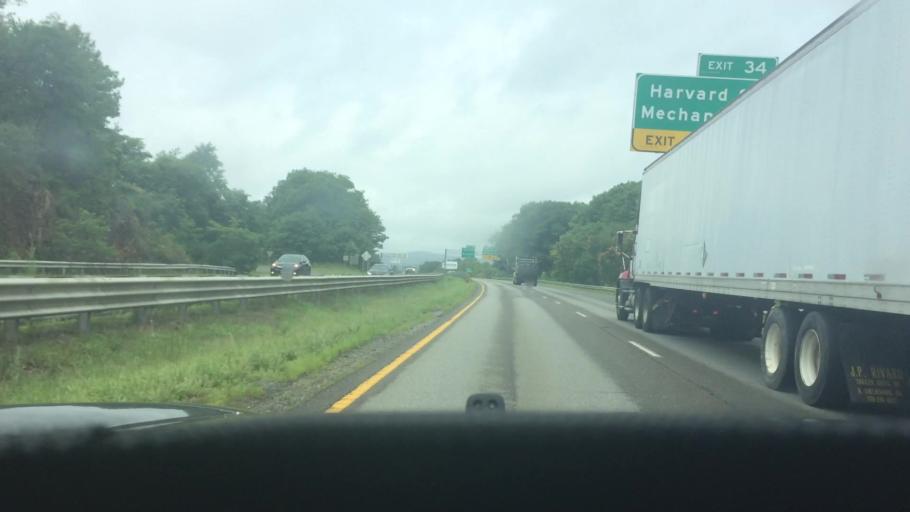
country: US
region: Massachusetts
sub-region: Worcester County
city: Leominster
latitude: 42.5214
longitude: -71.7046
